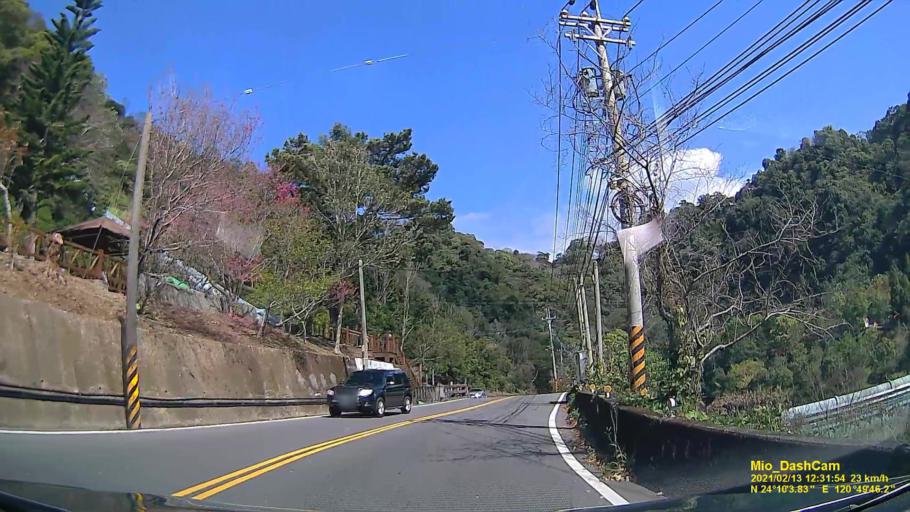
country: TW
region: Taiwan
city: Fengyuan
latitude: 24.1679
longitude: 120.8297
